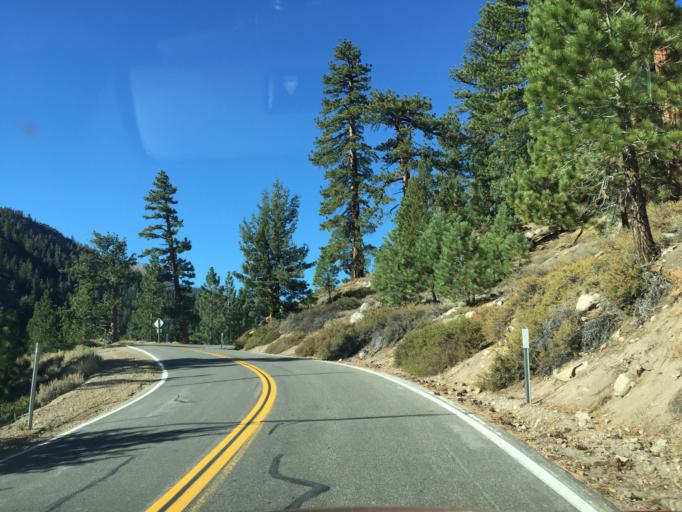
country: US
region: California
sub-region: Mono County
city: Bridgeport
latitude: 38.3210
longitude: -119.5643
